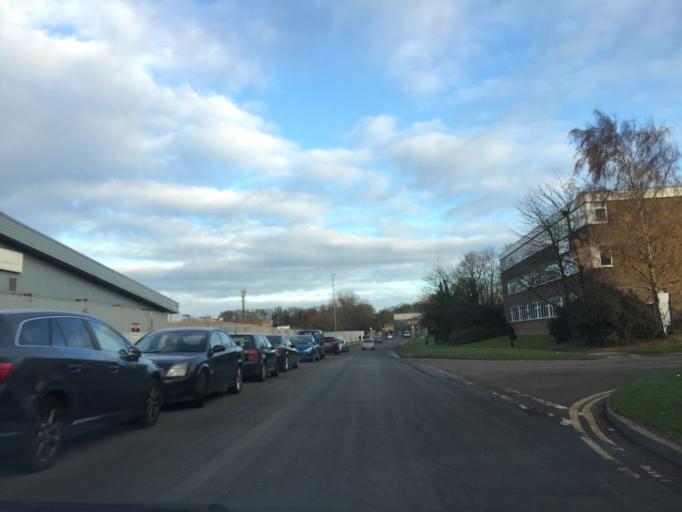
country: GB
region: England
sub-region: Northamptonshire
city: Northampton
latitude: 52.2759
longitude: -0.8689
